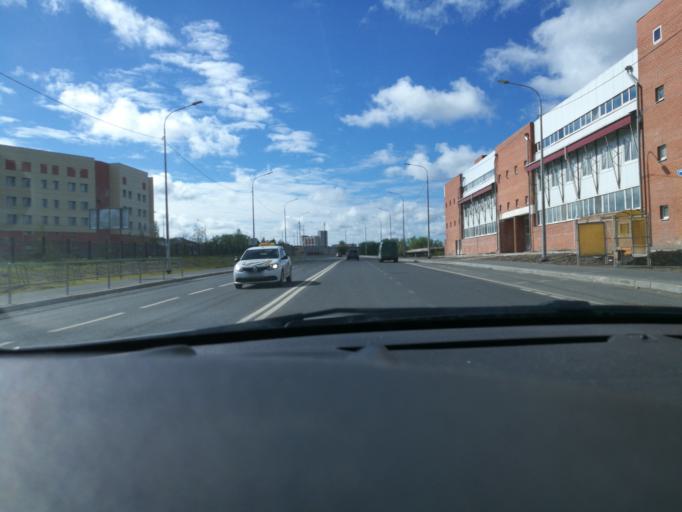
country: RU
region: Arkhangelskaya
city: Arkhangel'sk
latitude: 64.5651
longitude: 40.5516
